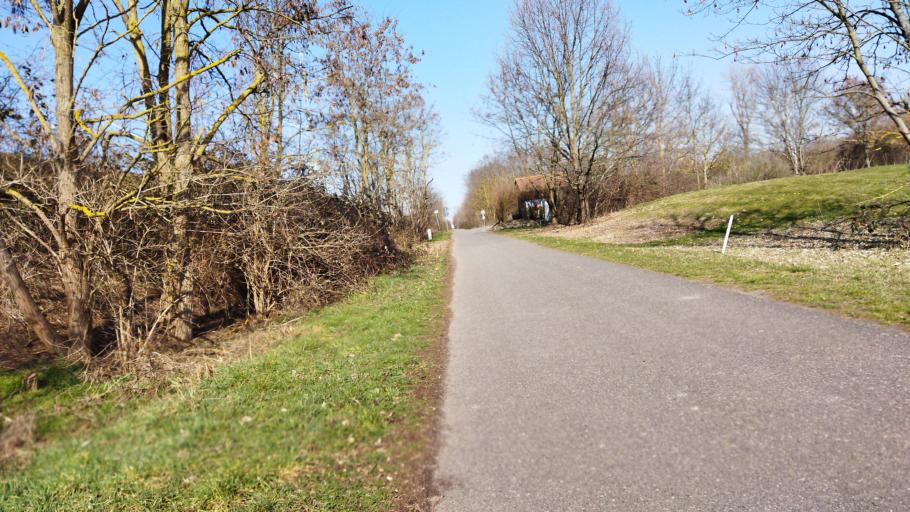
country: DE
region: Rheinland-Pfalz
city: Limburgerhof
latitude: 49.4075
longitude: 8.3774
